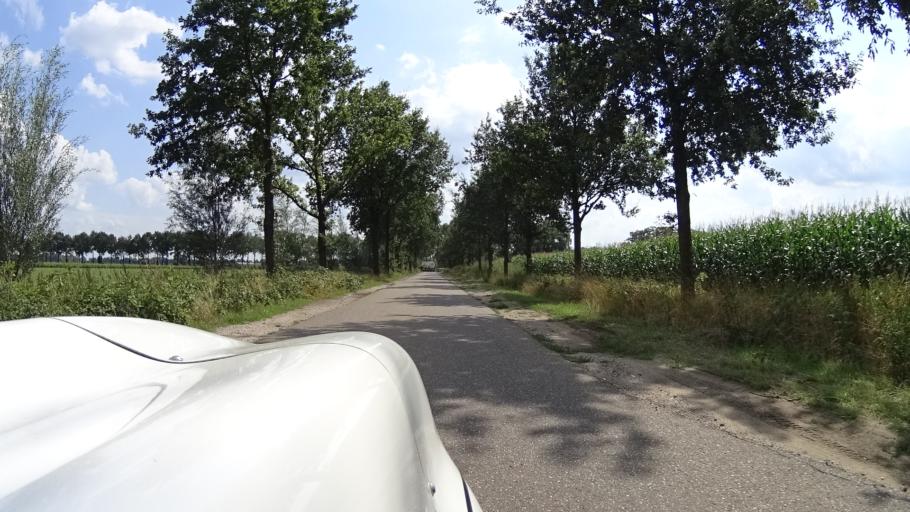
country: NL
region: North Brabant
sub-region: Gemeente Bernheze
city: Loosbroek
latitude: 51.6562
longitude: 5.5142
